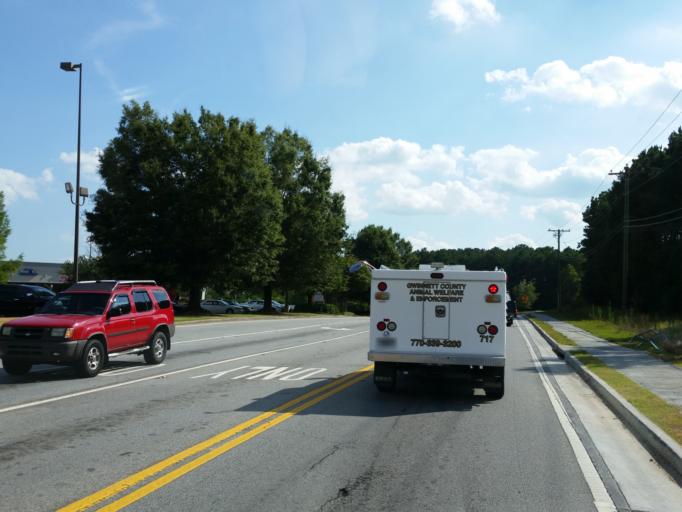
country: US
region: Georgia
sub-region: Gwinnett County
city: Lawrenceville
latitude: 33.9554
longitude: -84.0568
